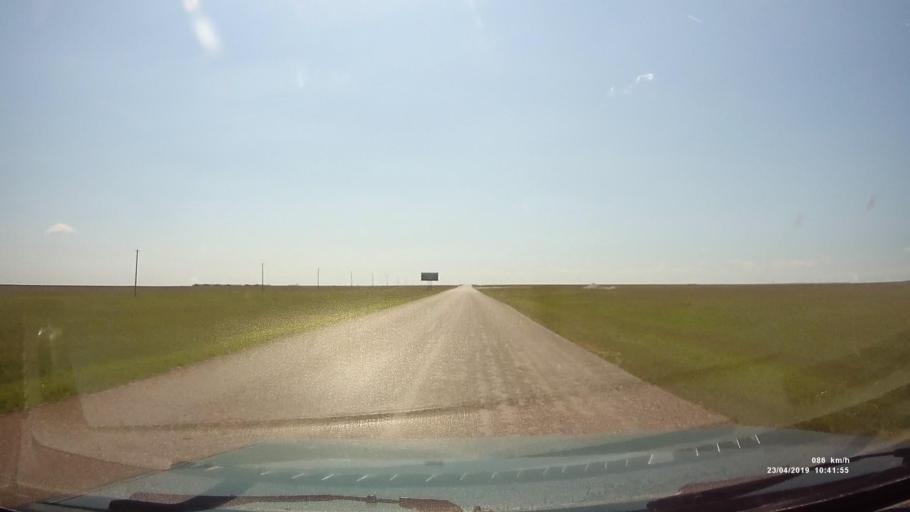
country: RU
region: Kalmykiya
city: Yashalta
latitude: 46.4886
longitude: 42.6403
